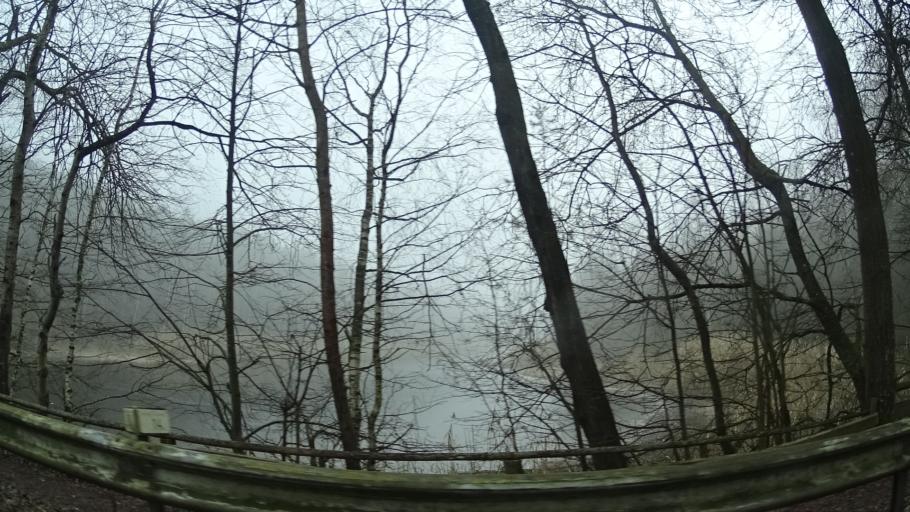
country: DE
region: Rheinland-Pfalz
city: Neuhemsbach
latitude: 49.5123
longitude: 7.9362
